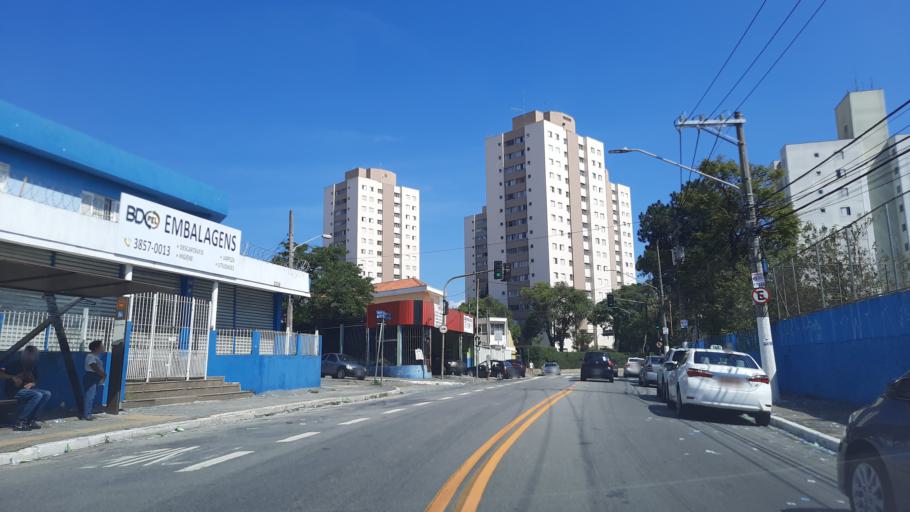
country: BR
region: Sao Paulo
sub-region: Sao Paulo
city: Sao Paulo
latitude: -23.4983
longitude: -46.6757
